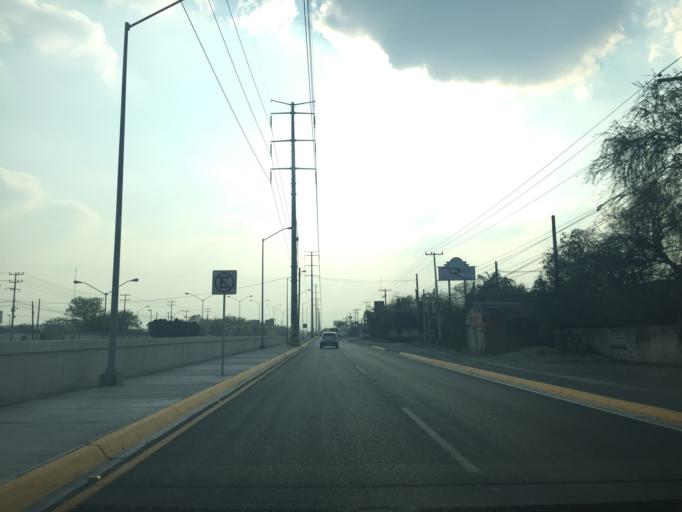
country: MX
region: Nuevo Leon
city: Apodaca
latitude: 25.7675
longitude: -100.1993
